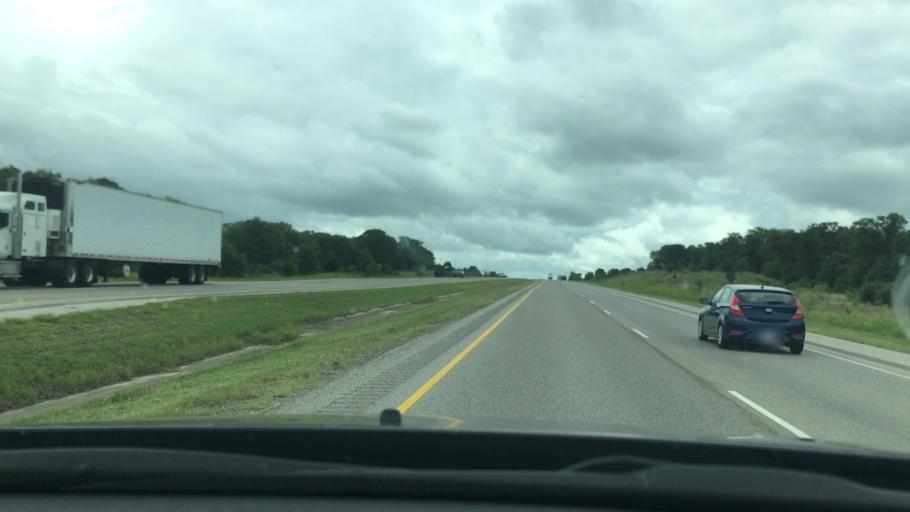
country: US
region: Oklahoma
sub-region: Carter County
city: Ardmore
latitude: 34.1296
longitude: -97.0810
